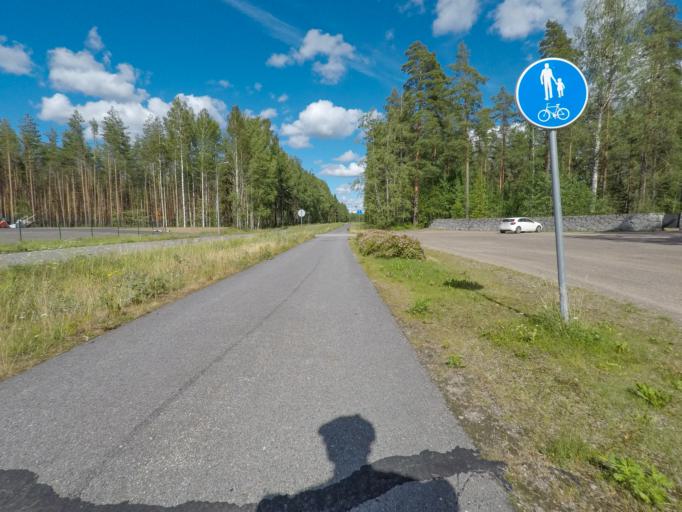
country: FI
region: South Karelia
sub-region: Lappeenranta
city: Lappeenranta
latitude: 61.0877
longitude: 28.3472
